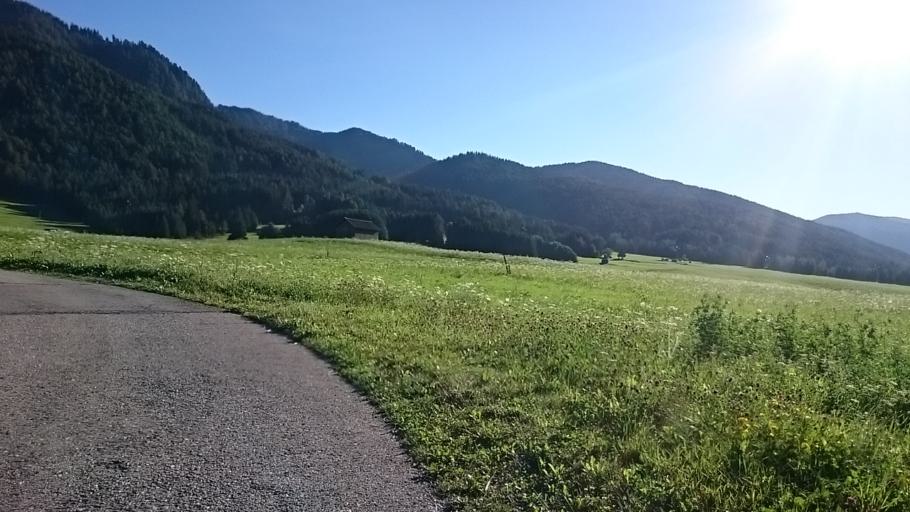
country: IT
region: Trentino-Alto Adige
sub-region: Bolzano
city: Villabassa
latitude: 46.7331
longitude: 12.1938
